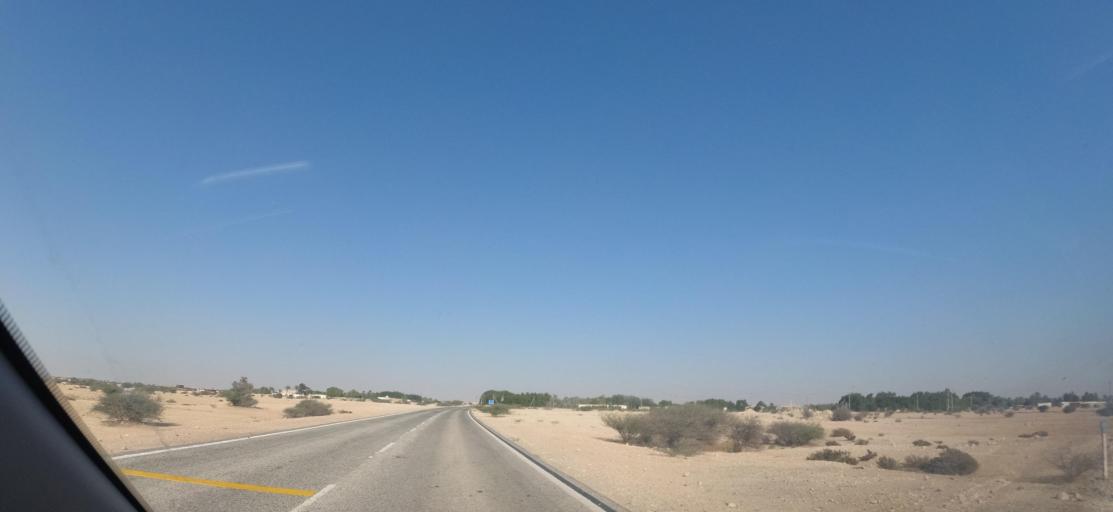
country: QA
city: Al Jumayliyah
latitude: 25.6230
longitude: 51.0887
